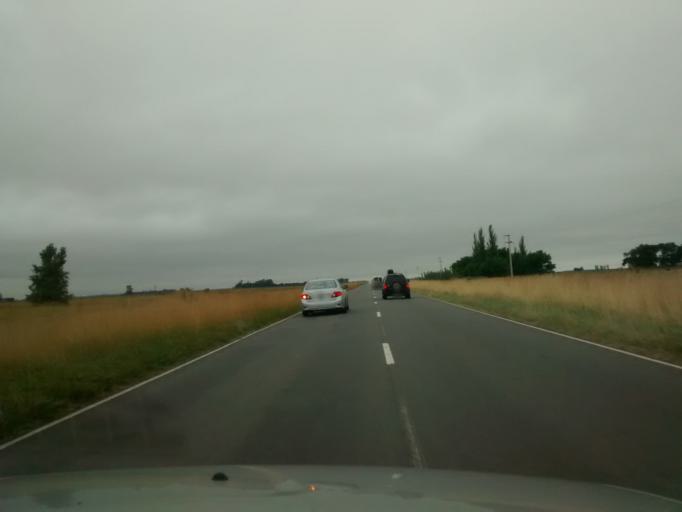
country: AR
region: Buenos Aires
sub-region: Partido de Ayacucho
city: Ayacucho
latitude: -37.0281
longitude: -58.5394
